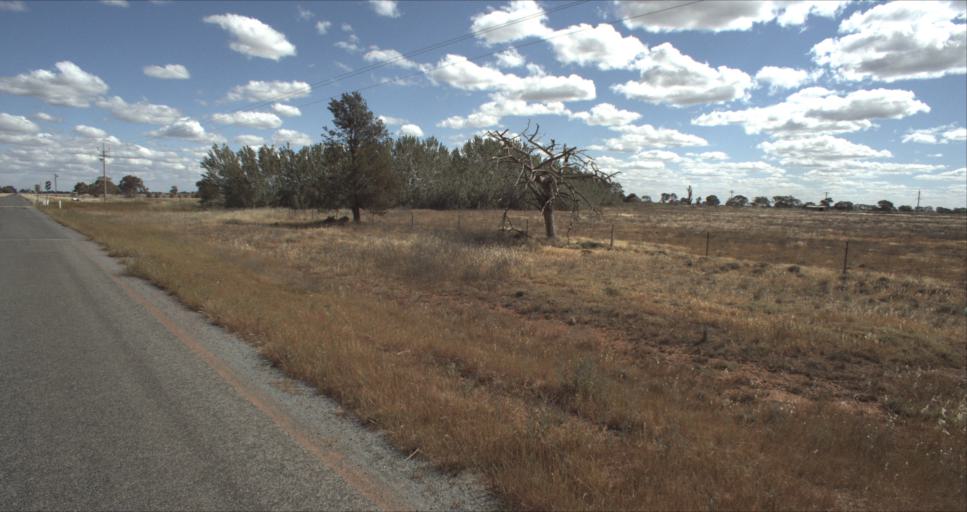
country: AU
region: New South Wales
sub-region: Leeton
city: Leeton
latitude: -34.4583
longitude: 146.2532
